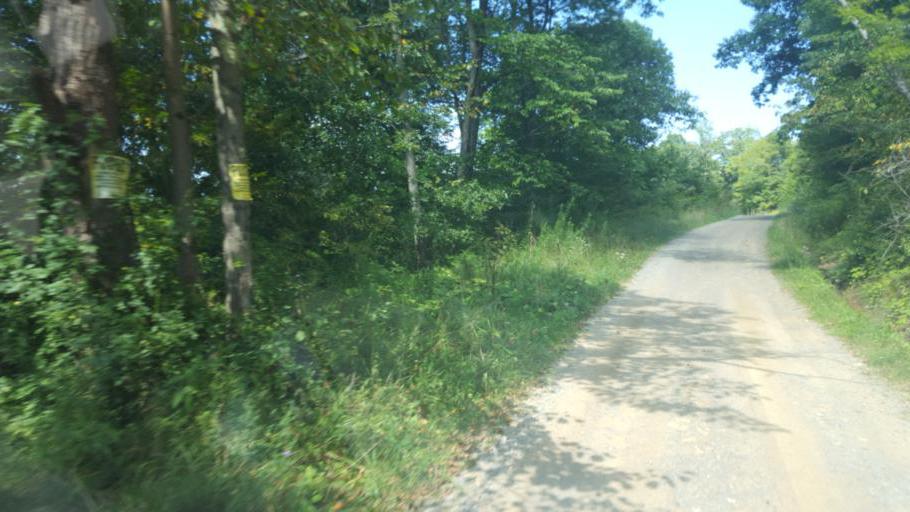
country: US
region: Pennsylvania
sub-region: Clarion County
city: Knox
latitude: 41.1122
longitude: -79.5384
